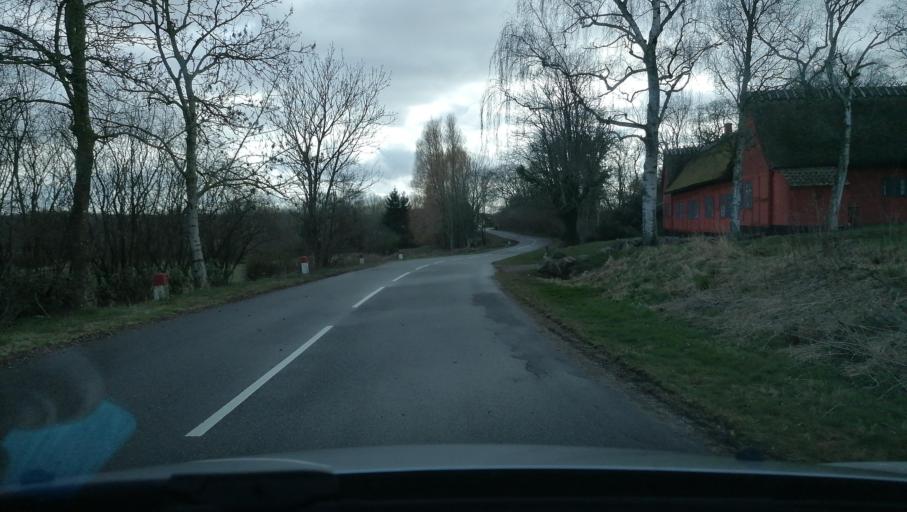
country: DK
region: Zealand
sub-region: Odsherred Kommune
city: Horve
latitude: 55.7829
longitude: 11.4016
